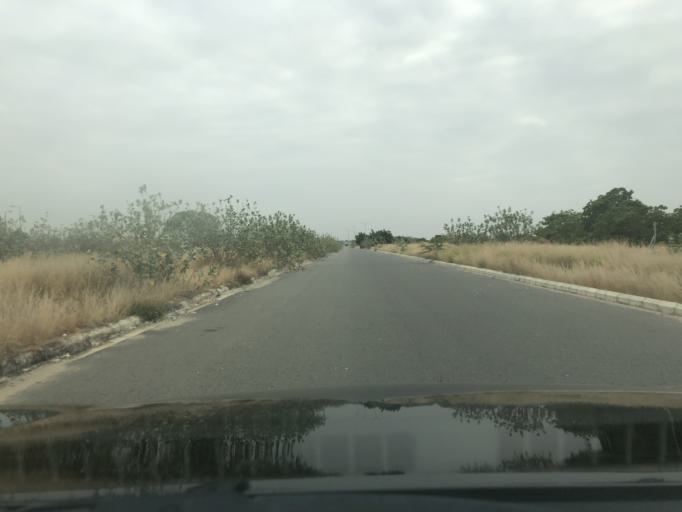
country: AO
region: Luanda
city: Luanda
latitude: -8.9527
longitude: 13.2493
